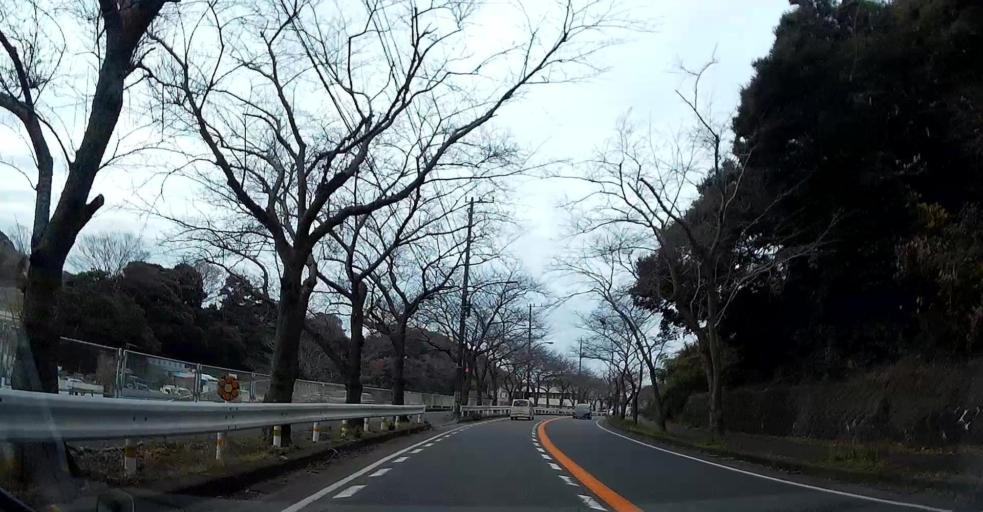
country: JP
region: Kanagawa
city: Yokosuka
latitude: 35.2185
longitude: 139.6715
